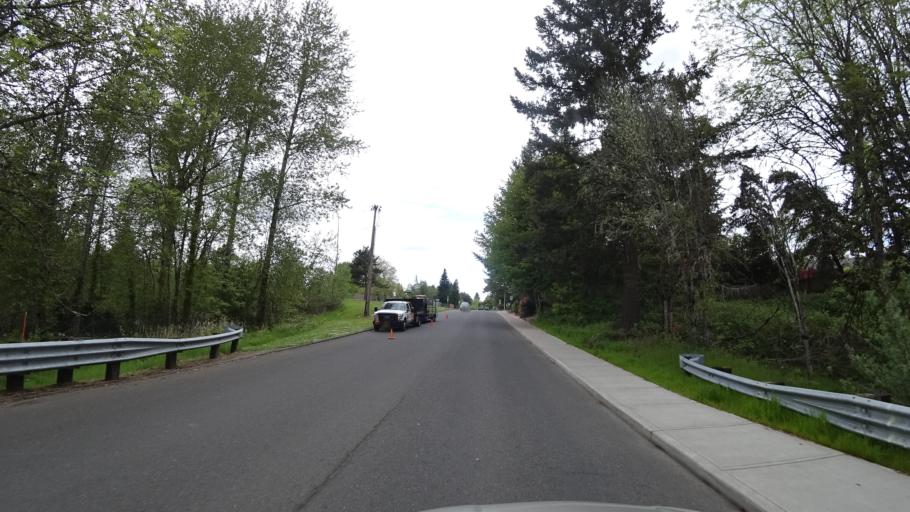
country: US
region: Oregon
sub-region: Washington County
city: Rockcreek
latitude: 45.5494
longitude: -122.8833
